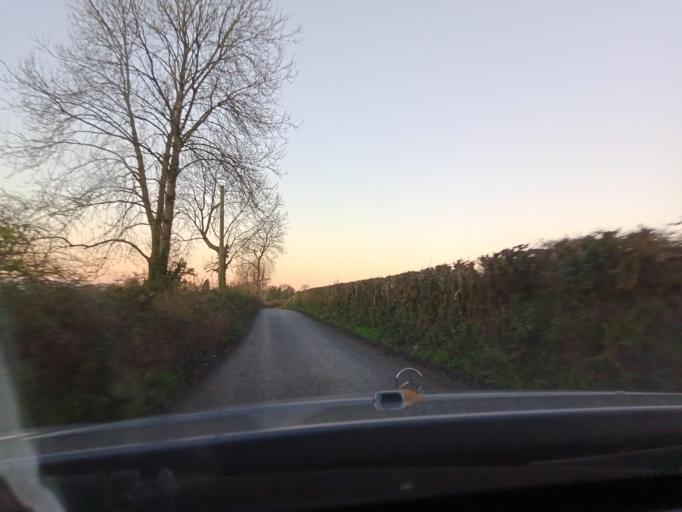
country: IE
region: Leinster
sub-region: Kilkenny
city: Thomastown
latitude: 52.4679
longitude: -7.0985
